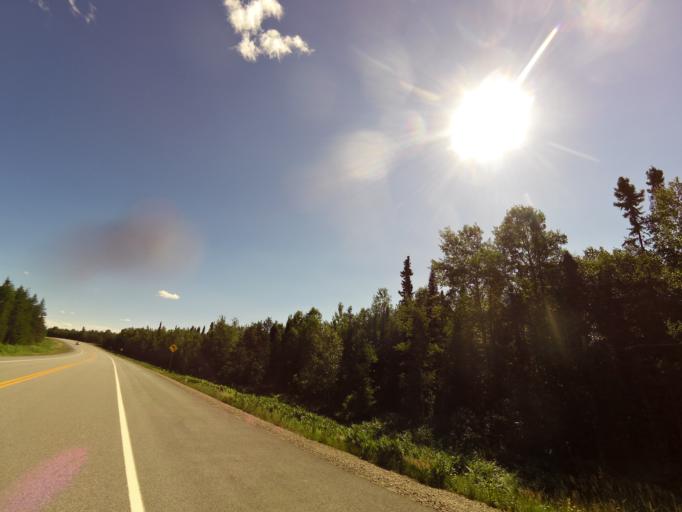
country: CA
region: Quebec
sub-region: Abitibi-Temiscamingue
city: Val-d'Or
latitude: 47.8653
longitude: -77.3551
